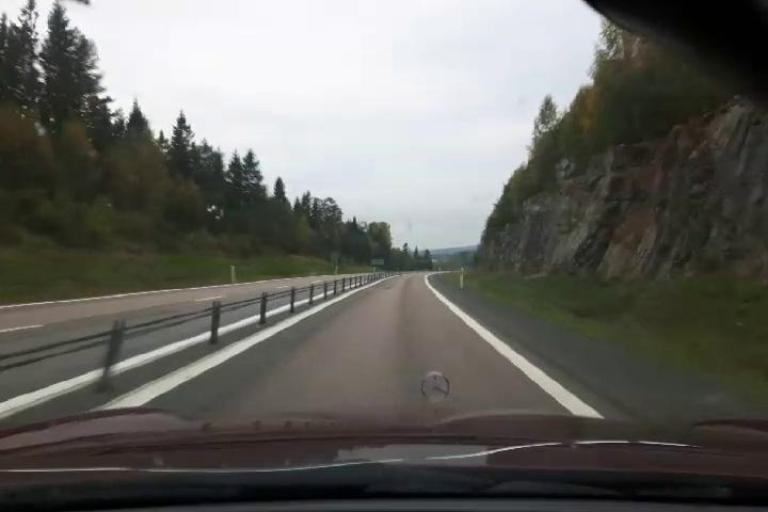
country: SE
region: Vaesternorrland
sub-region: Haernoesands Kommun
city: Haernoesand
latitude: 62.8596
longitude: 18.0254
